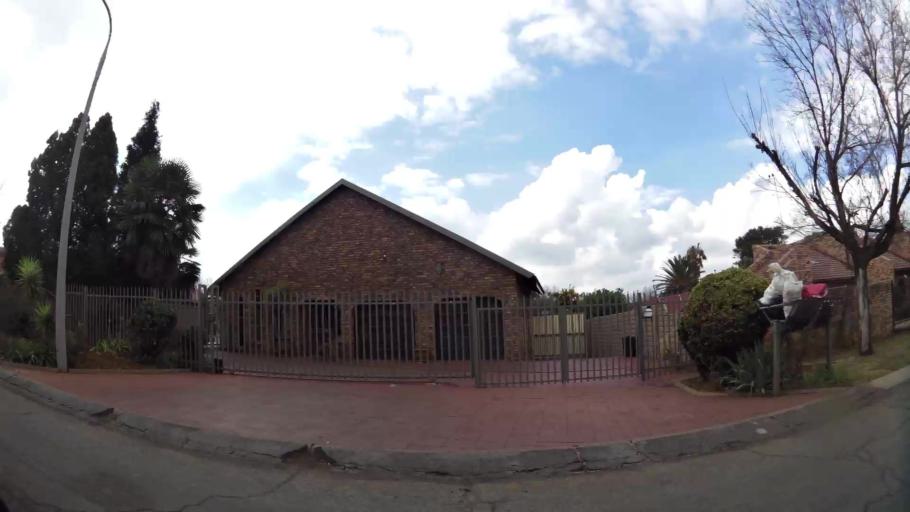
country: ZA
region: Gauteng
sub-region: Sedibeng District Municipality
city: Vanderbijlpark
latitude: -26.7352
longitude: 27.8524
